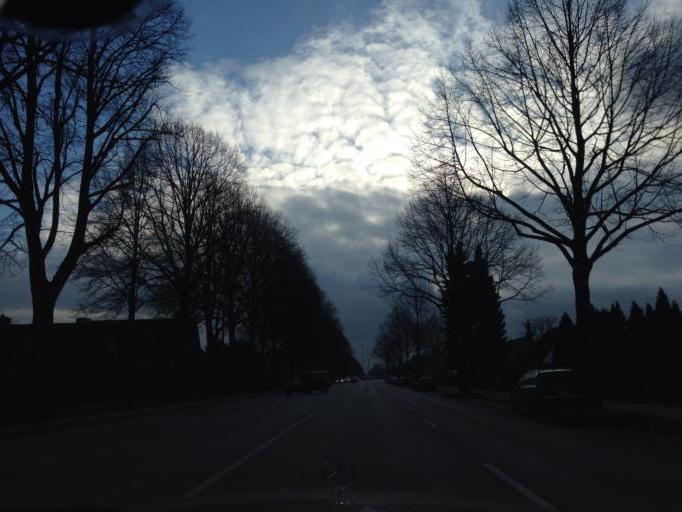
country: DE
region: Hamburg
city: Wandsbek
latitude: 53.5600
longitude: 10.1180
